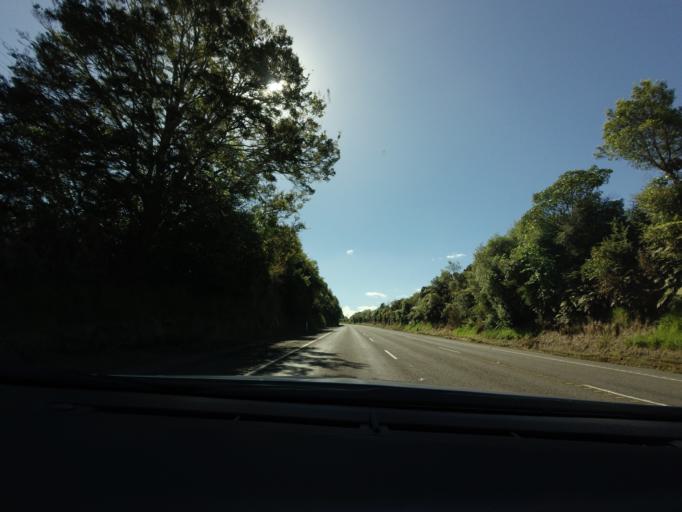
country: NZ
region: Bay of Plenty
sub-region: Rotorua District
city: Rotorua
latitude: -38.0743
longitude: 176.1778
